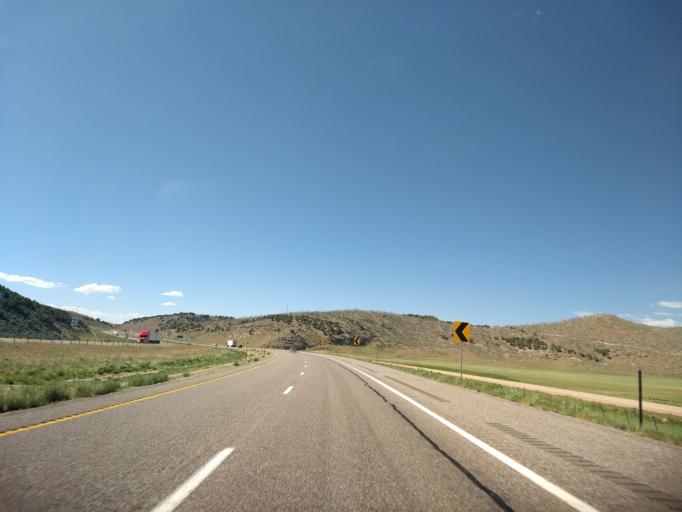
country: US
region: Utah
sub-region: Beaver County
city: Beaver
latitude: 38.6708
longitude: -112.5884
